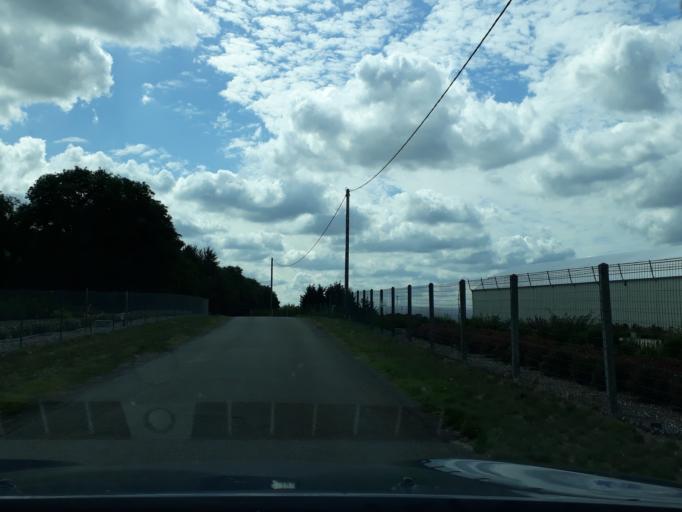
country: FR
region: Centre
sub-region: Departement du Loiret
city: Saint-Cyr-en-Val
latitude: 47.8513
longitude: 1.9765
